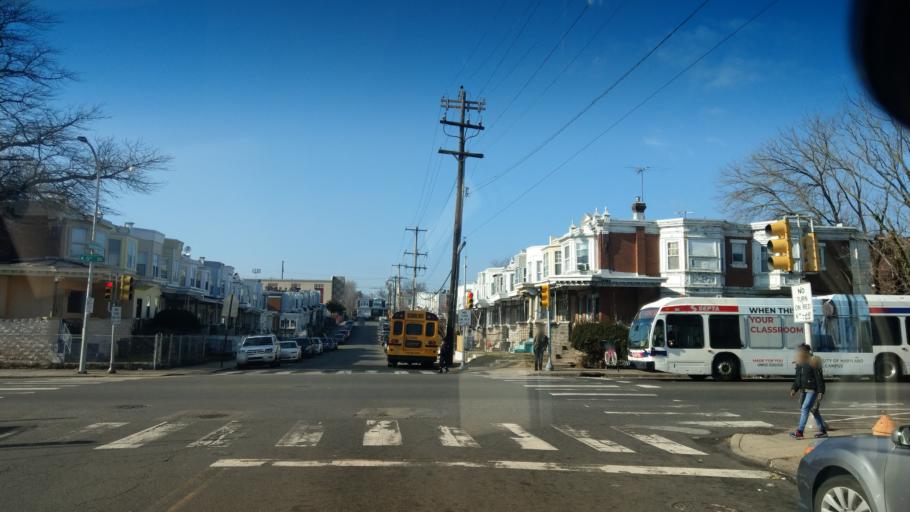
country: US
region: Pennsylvania
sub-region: Montgomery County
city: Jenkintown
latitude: 40.0303
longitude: -75.1316
